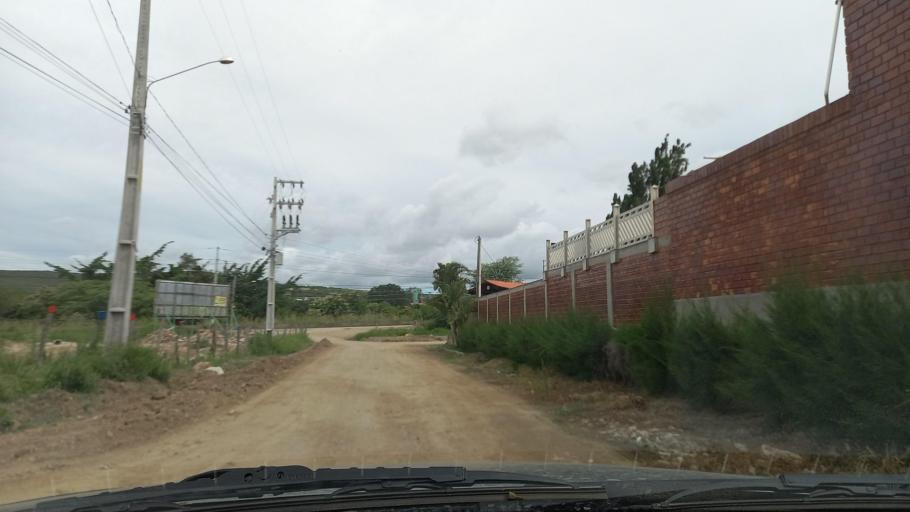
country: BR
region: Pernambuco
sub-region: Gravata
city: Gravata
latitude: -8.2040
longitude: -35.6008
